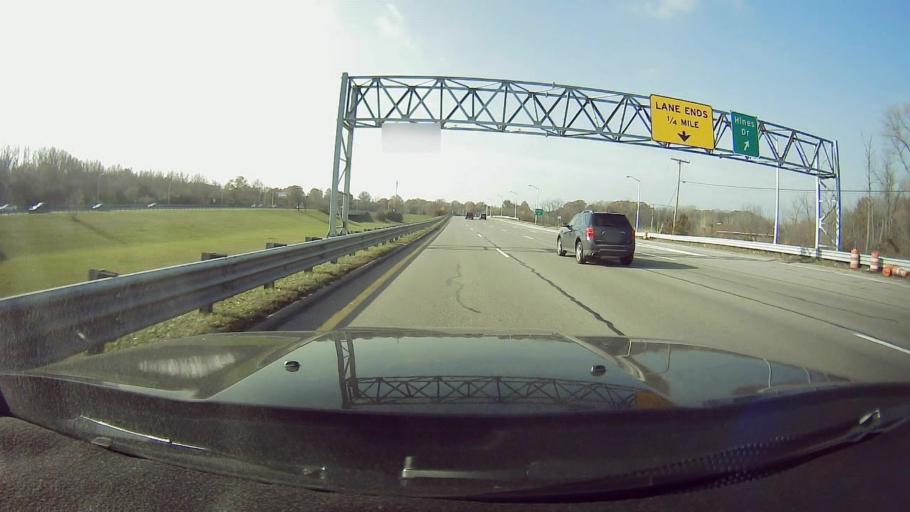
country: US
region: Michigan
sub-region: Wayne County
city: Dearborn Heights
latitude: 42.3281
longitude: -83.2425
